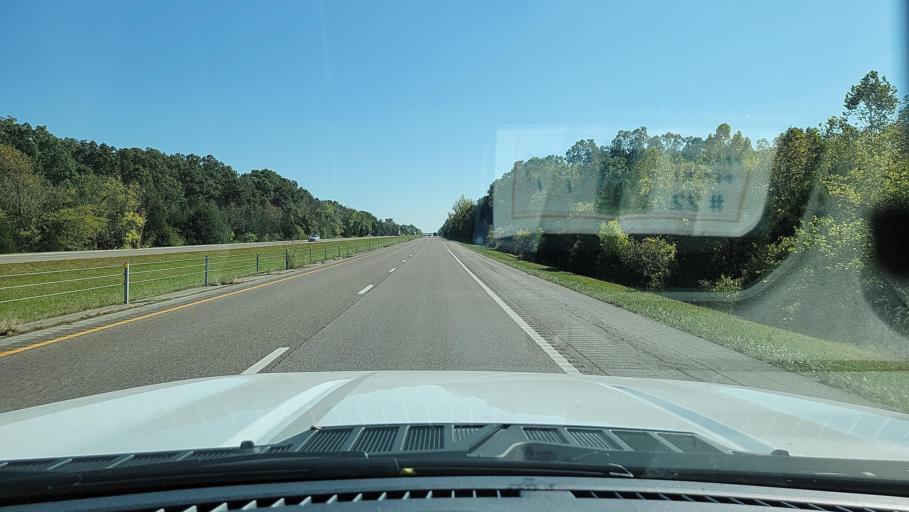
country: US
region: Missouri
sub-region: Jefferson County
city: Crystal City
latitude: 38.1247
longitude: -90.3116
